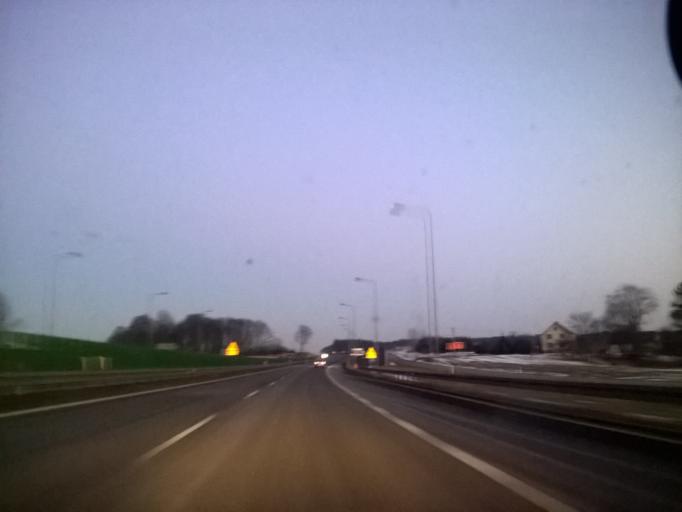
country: PL
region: Warmian-Masurian Voivodeship
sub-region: Powiat olsztynski
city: Biskupiec
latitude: 53.8488
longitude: 20.9736
